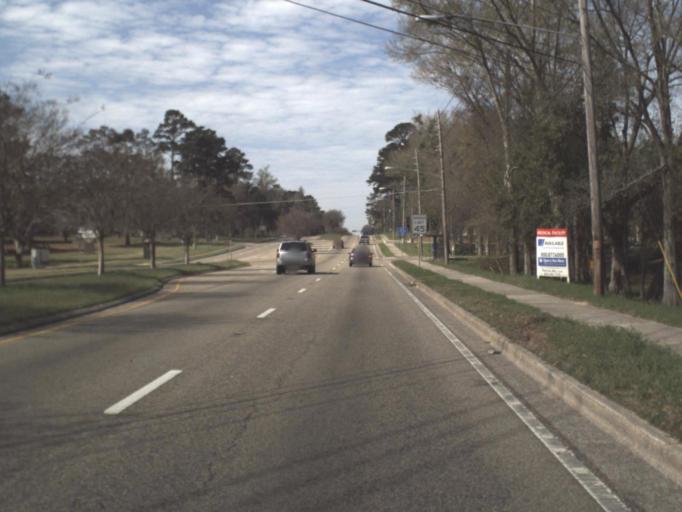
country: US
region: Florida
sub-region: Leon County
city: Tallahassee
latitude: 30.4561
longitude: -84.2392
